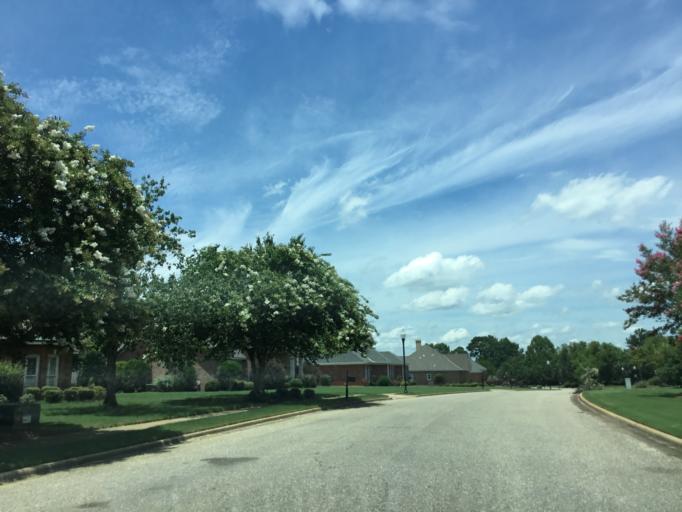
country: US
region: Alabama
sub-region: Montgomery County
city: Pike Road
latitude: 32.3760
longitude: -86.1353
